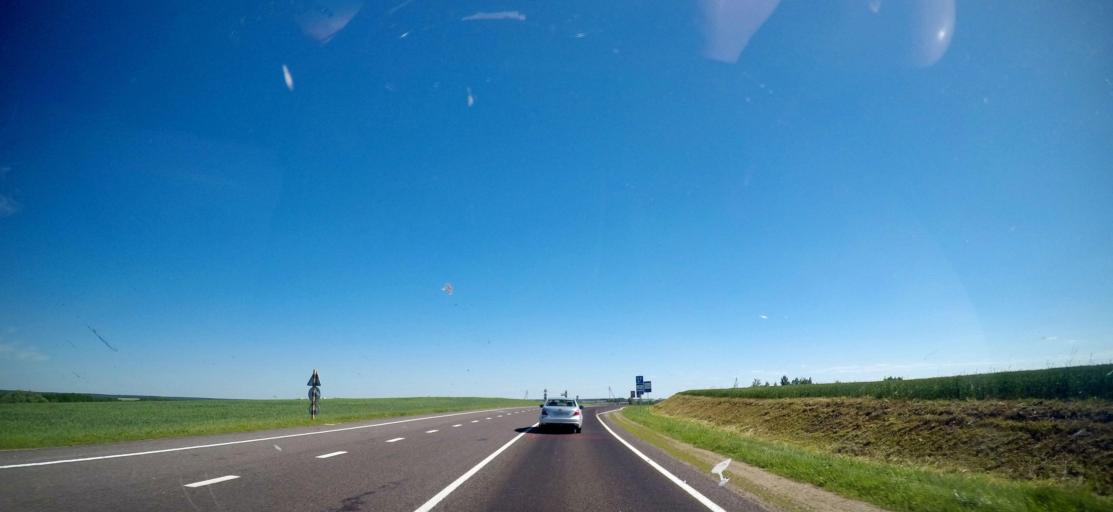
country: BY
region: Grodnenskaya
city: Vyalikaya Byerastavitsa
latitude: 53.2088
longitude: 24.0060
